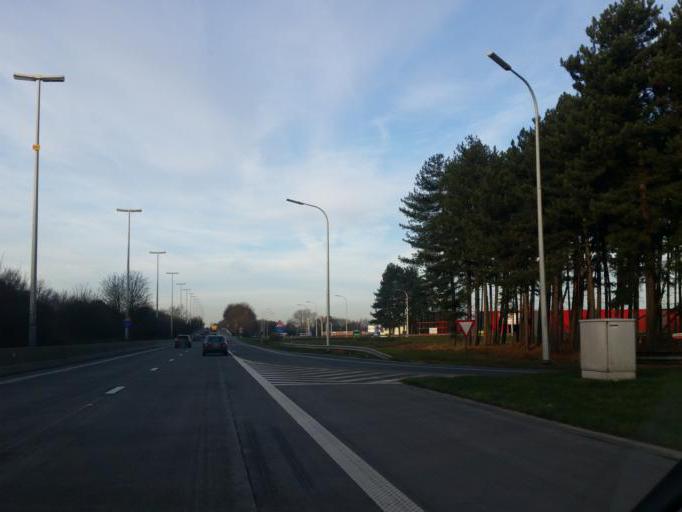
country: BE
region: Flanders
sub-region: Provincie Oost-Vlaanderen
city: Zelzate
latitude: 51.1912
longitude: 3.8388
